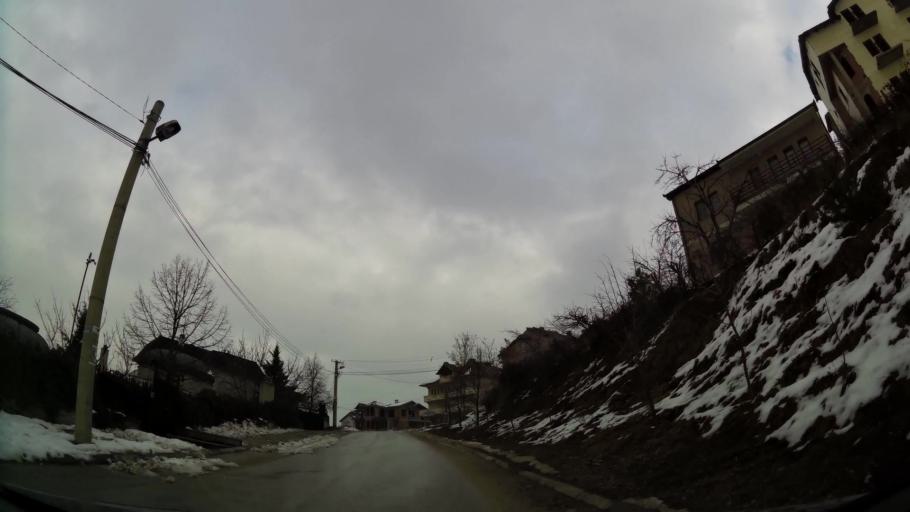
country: XK
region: Pristina
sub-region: Komuna e Prishtines
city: Pristina
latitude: 42.6763
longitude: 21.1830
